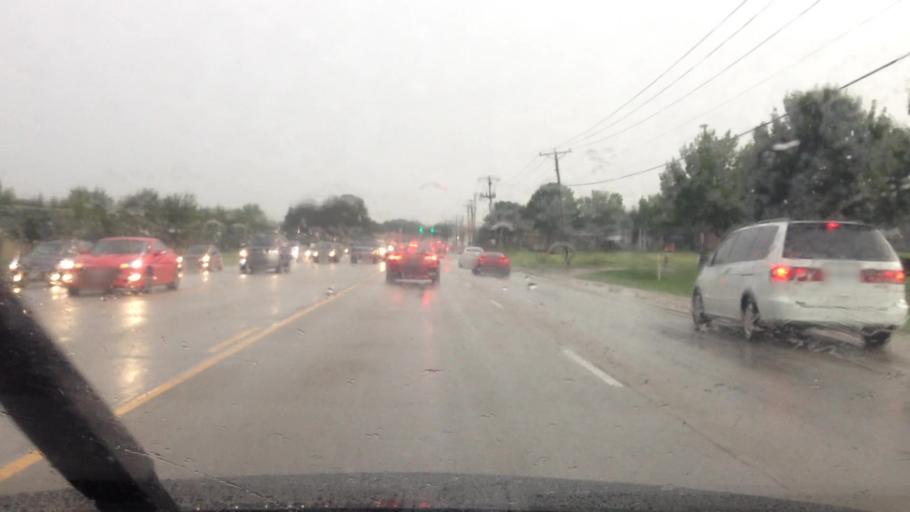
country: US
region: Texas
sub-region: Tarrant County
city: North Richland Hills
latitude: 32.8458
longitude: -97.1983
